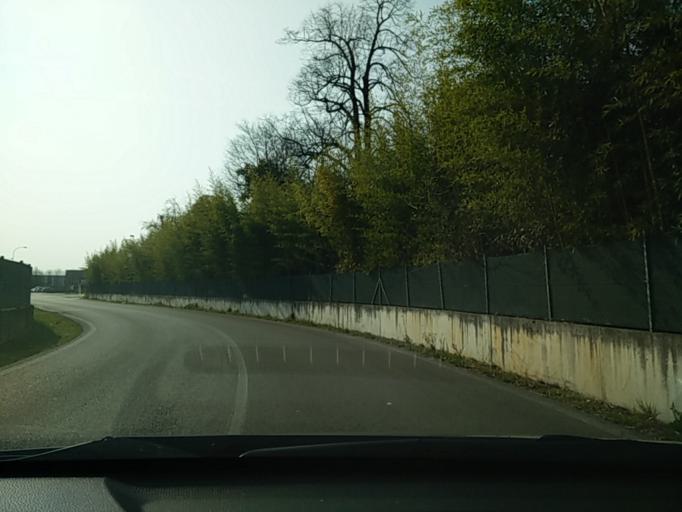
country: IT
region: Veneto
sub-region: Provincia di Treviso
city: Volpago del Montello
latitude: 45.7763
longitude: 12.1072
